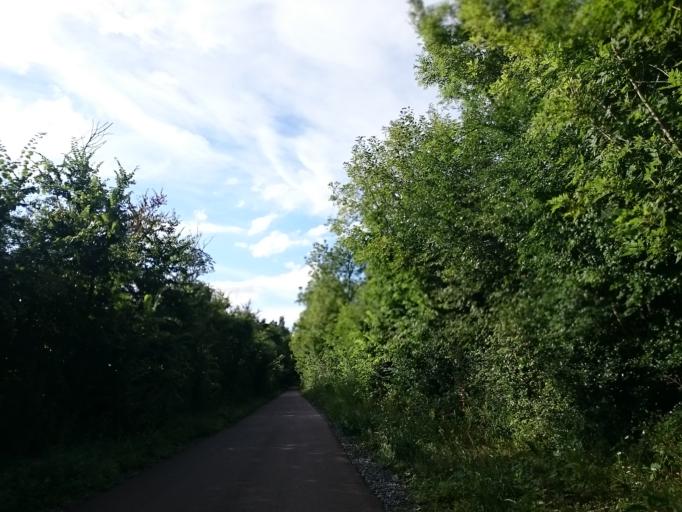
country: FR
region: Lower Normandy
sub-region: Departement du Calvados
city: Saint-Andre-sur-Orne
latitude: 49.1156
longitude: -0.3903
